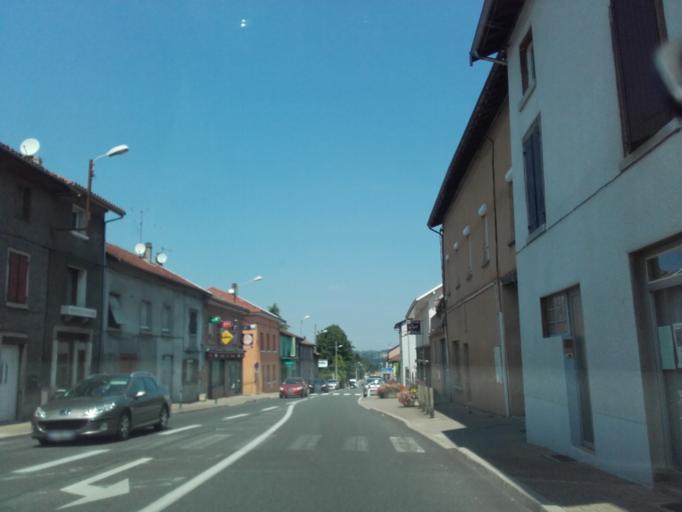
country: FR
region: Rhone-Alpes
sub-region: Departement de l'Isere
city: Nivolas-Vermelle
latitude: 45.5569
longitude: 5.3050
